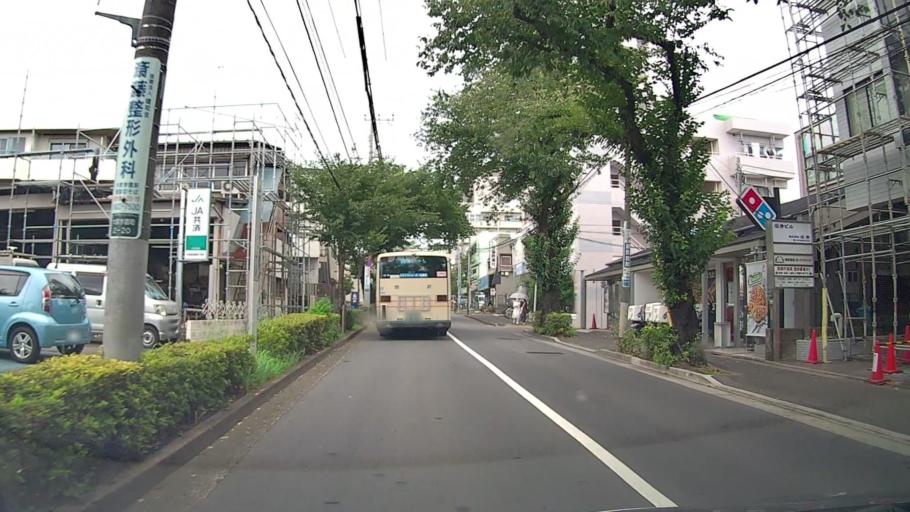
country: JP
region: Saitama
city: Wako
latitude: 35.7598
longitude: 139.5886
